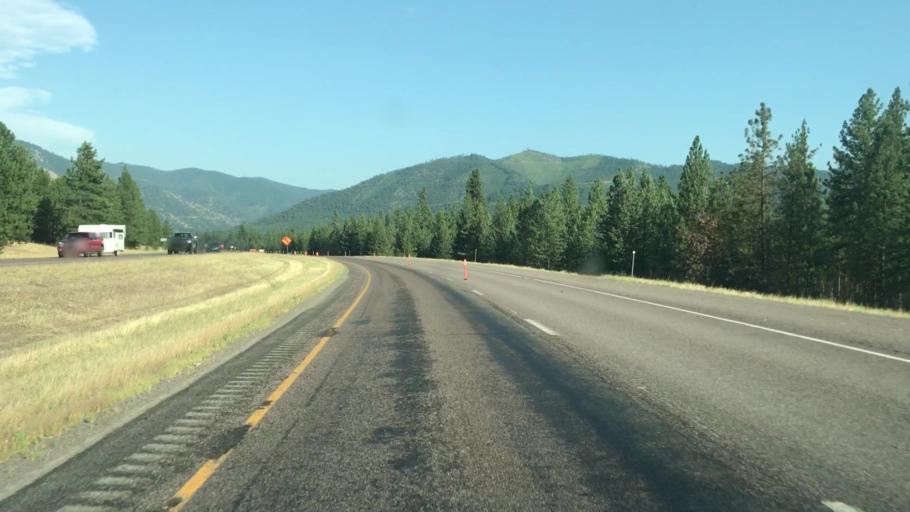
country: US
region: Montana
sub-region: Mineral County
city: Superior
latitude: 47.0153
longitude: -114.7333
